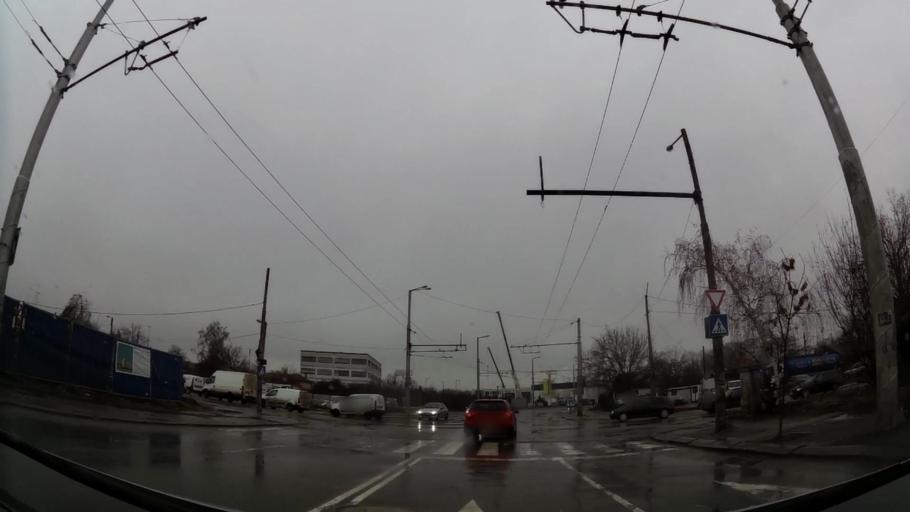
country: BG
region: Sofia-Capital
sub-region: Stolichna Obshtina
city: Sofia
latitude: 42.6404
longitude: 23.4127
